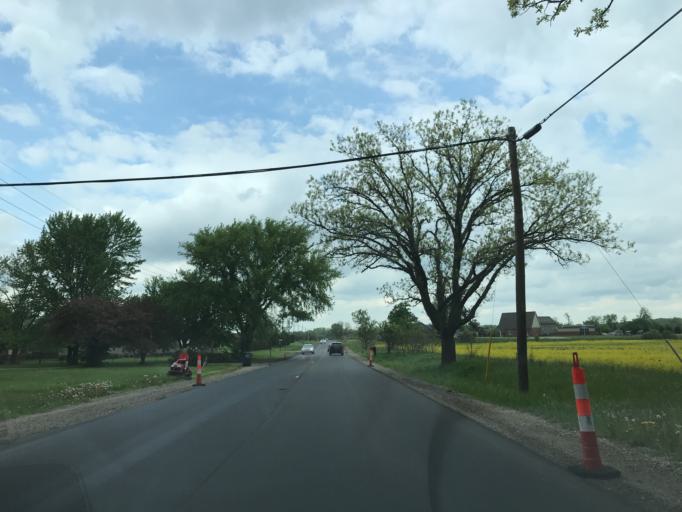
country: US
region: Michigan
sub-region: Oakland County
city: South Lyon
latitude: 42.4964
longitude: -83.6537
